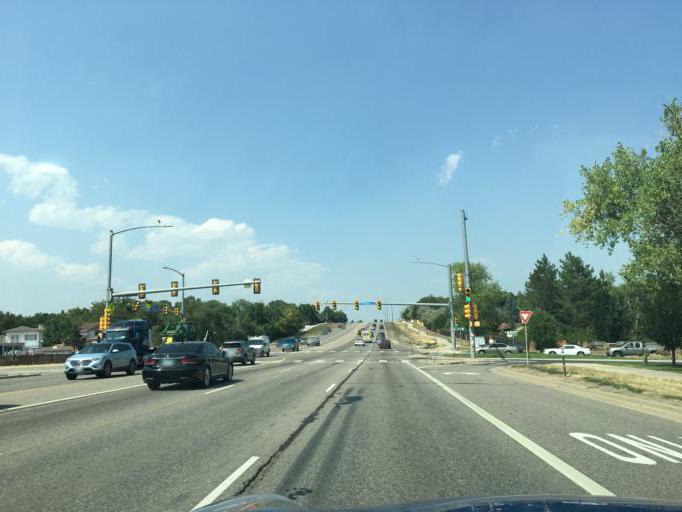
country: US
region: Colorado
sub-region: Jefferson County
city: Arvada
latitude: 39.8463
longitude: -105.0817
